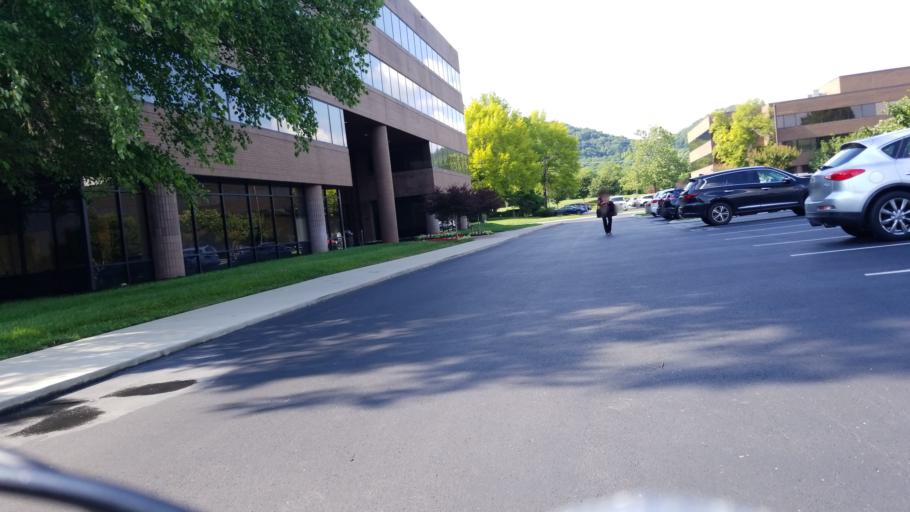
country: US
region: Tennessee
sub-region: Williamson County
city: Brentwood
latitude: 36.0364
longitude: -86.8029
